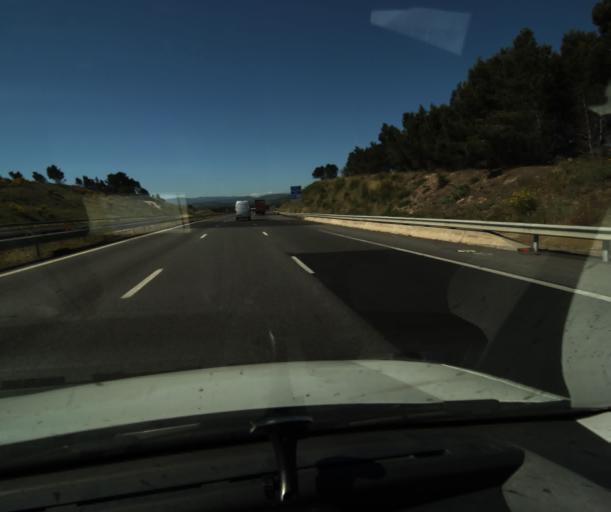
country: FR
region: Languedoc-Roussillon
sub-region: Departement de l'Aude
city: Peyriac-de-Mer
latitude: 43.1193
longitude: 2.9579
